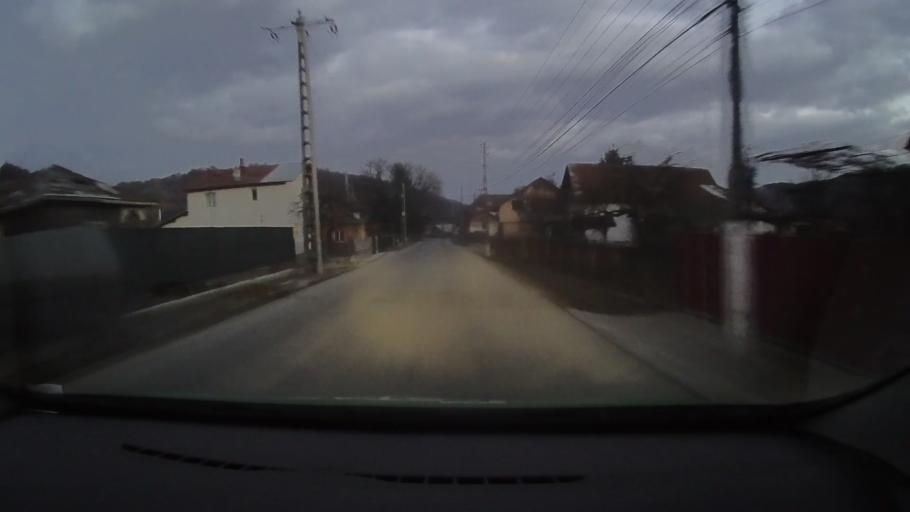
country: RO
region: Prahova
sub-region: Comuna Provita de Sus
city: Provita de Sus
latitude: 45.1301
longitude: 25.6459
